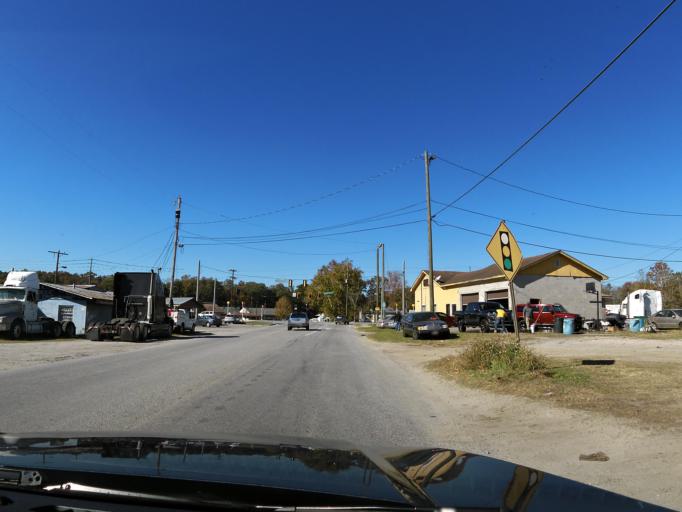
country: US
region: Georgia
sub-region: Chatham County
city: Garden City
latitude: 32.0921
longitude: -81.1488
